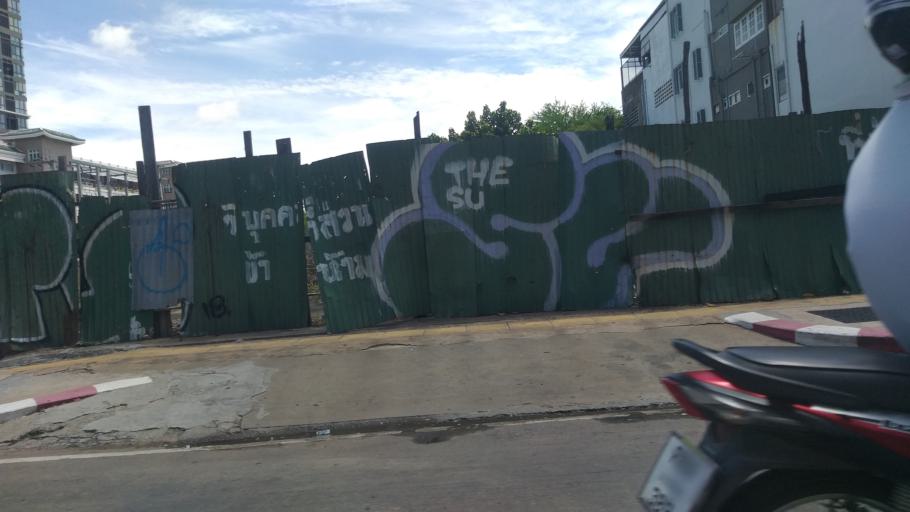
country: TH
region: Khon Kaen
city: Khon Kaen
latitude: 16.4309
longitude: 102.8319
